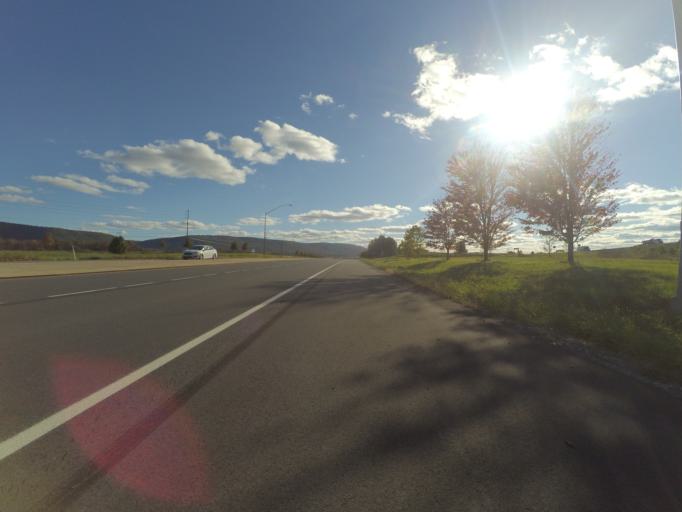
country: US
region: Pennsylvania
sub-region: Centre County
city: Pleasant Gap
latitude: 40.8711
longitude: -77.7792
